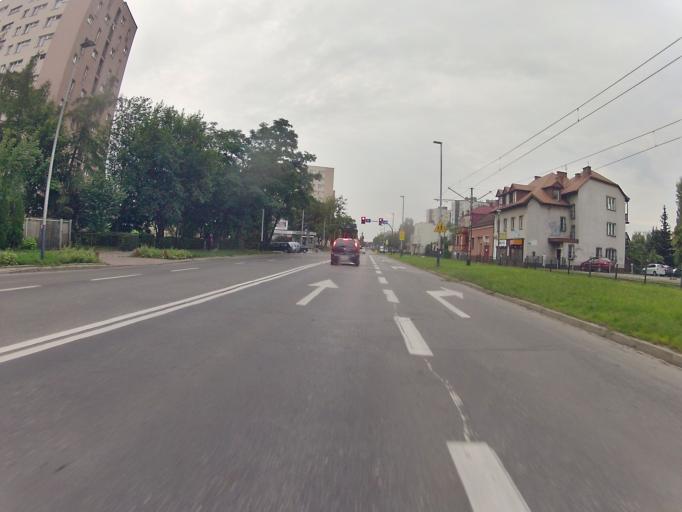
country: PL
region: Lesser Poland Voivodeship
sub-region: Krakow
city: Krakow
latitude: 50.0805
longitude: 19.8936
